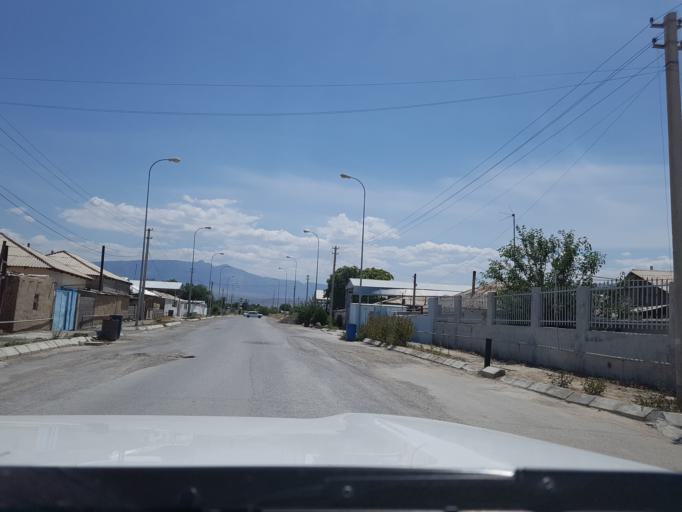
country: TM
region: Ahal
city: Abadan
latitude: 38.1658
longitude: 57.9594
